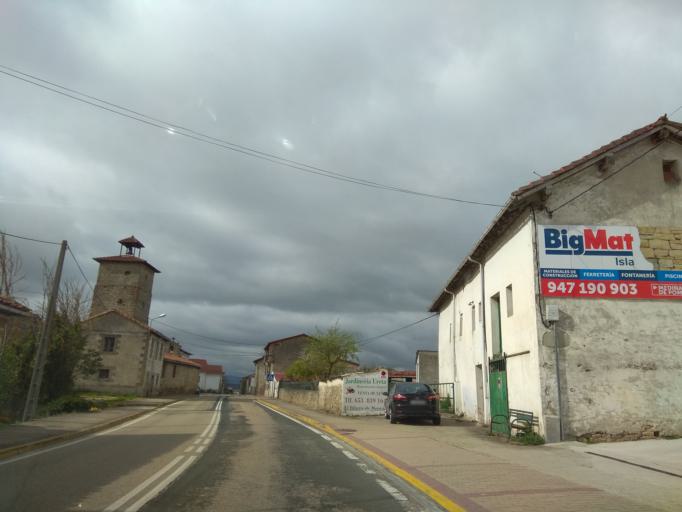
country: ES
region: Castille and Leon
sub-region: Provincia de Burgos
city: Espinosa de los Monteros
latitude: 43.0675
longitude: -3.4732
